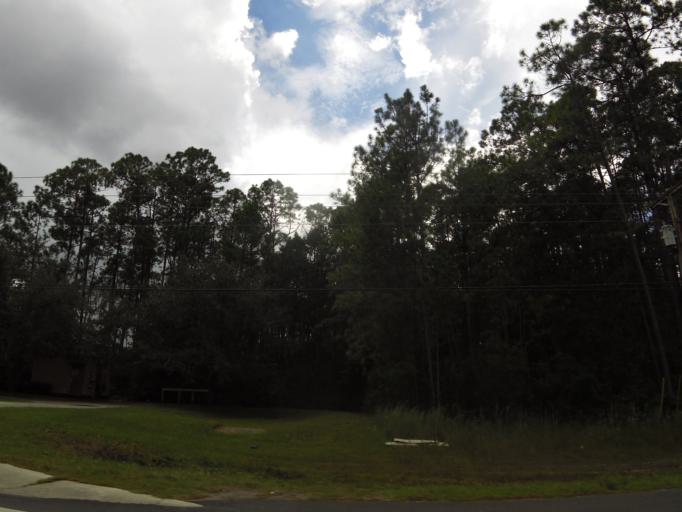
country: US
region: Florida
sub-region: Clay County
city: Middleburg
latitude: 30.0709
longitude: -81.9301
